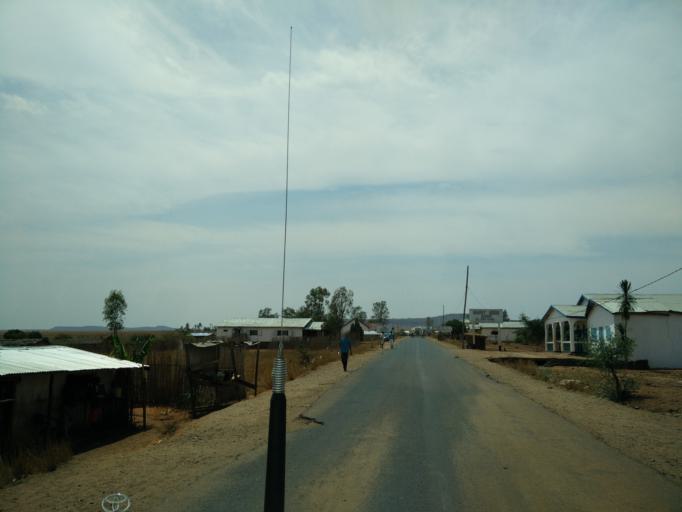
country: MG
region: Ihorombe
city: Ranohira
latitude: -22.7721
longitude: 45.1092
